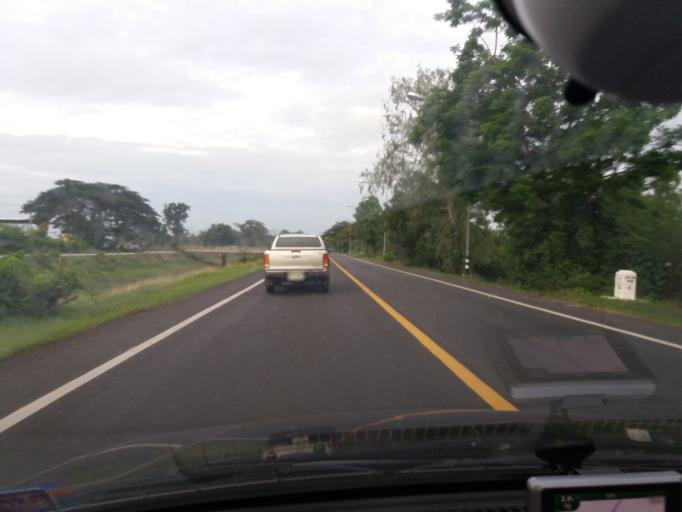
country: TH
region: Suphan Buri
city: Don Chedi
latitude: 14.5248
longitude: 99.9281
